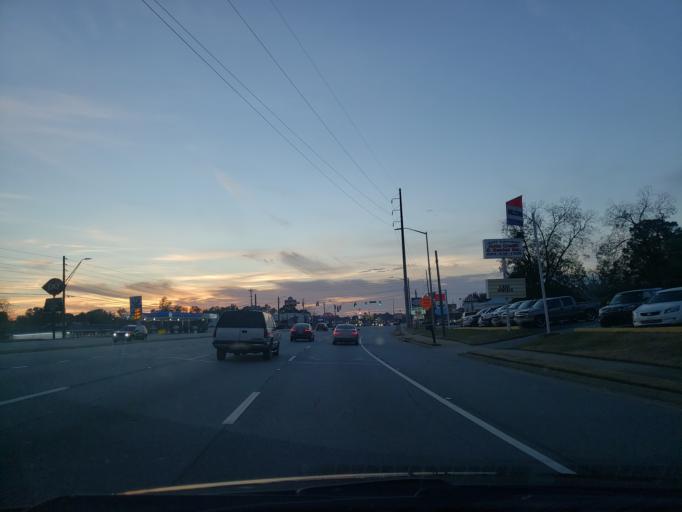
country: US
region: Georgia
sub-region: Dougherty County
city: Albany
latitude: 31.5711
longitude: -84.1028
